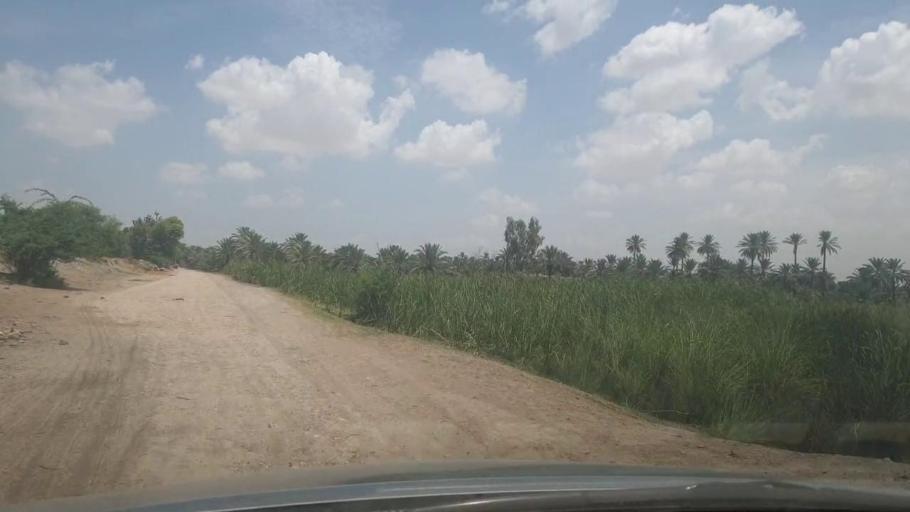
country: PK
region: Sindh
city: Kot Diji
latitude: 27.4218
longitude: 68.7386
